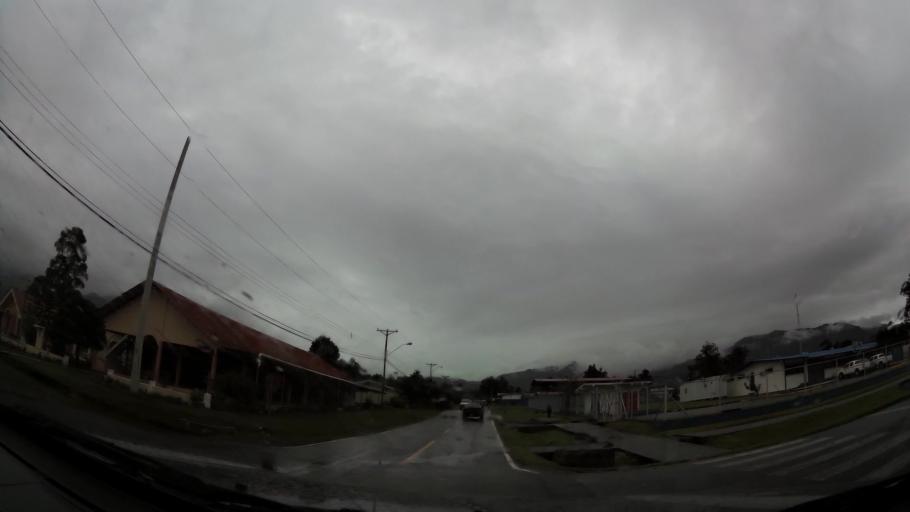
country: PA
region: Chiriqui
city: Volcan
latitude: 8.7867
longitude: -82.6505
